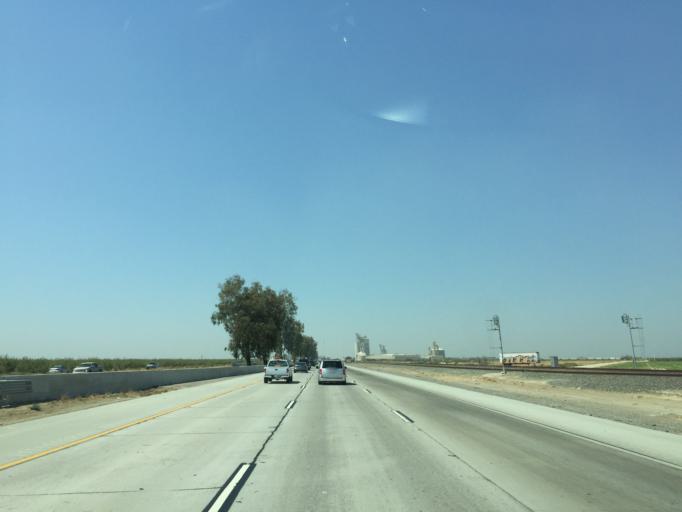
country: US
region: California
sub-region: Tulare County
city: London
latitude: 36.4321
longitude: -119.4746
